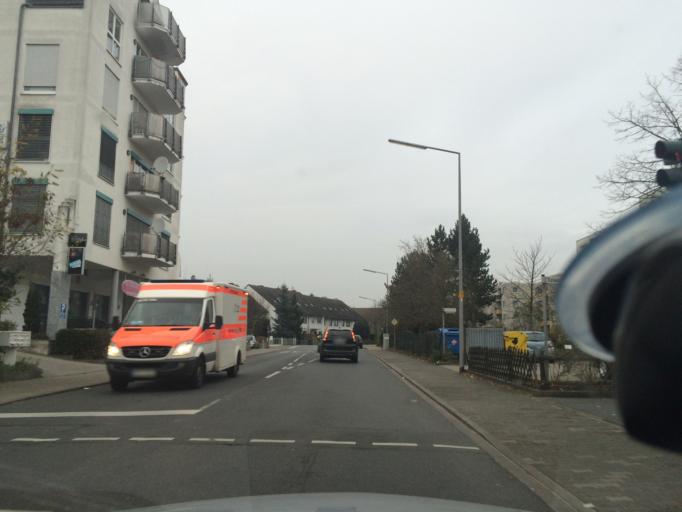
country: DE
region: Hesse
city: Morfelden-Walldorf
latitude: 49.9789
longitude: 8.5631
